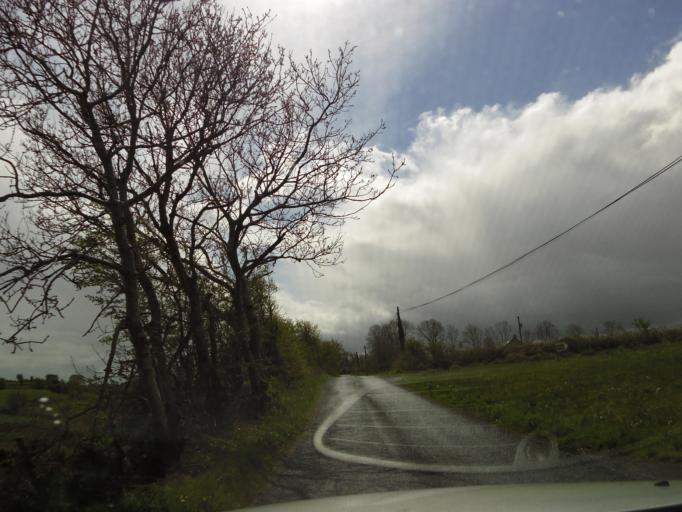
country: IE
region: Connaught
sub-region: Maigh Eo
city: Kiltamagh
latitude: 53.7963
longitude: -8.9659
